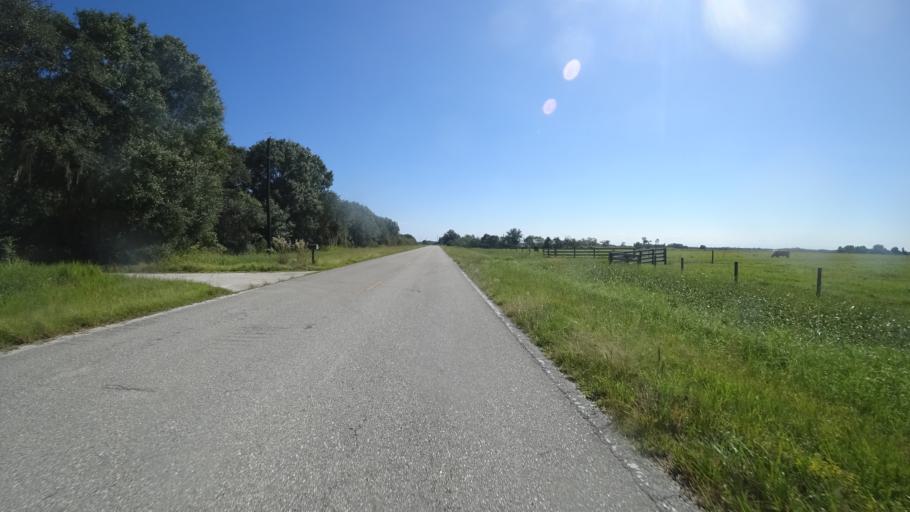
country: US
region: Florida
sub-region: DeSoto County
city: Nocatee
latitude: 27.2701
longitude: -82.0961
